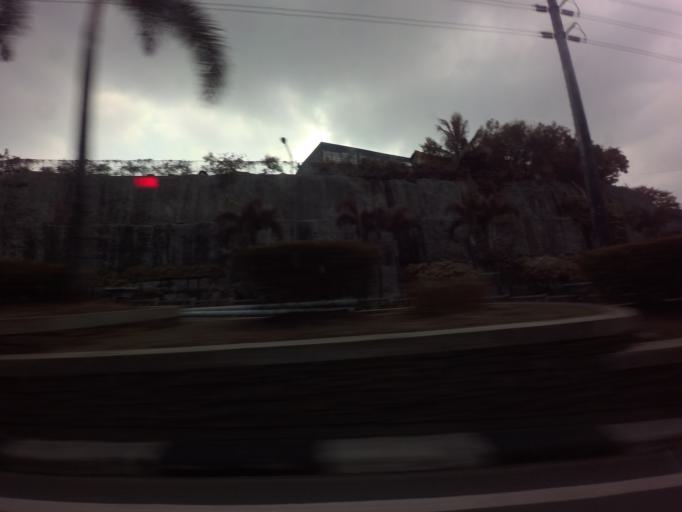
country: PH
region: Calabarzon
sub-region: Province of Rizal
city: Pateros
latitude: 14.5575
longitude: 121.0619
